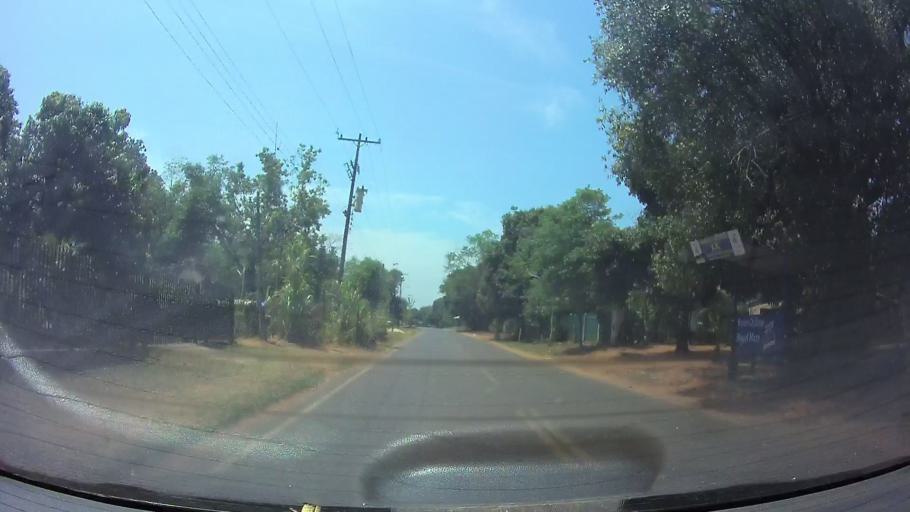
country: PY
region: Central
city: Ita
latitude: -25.4379
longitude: -57.3992
